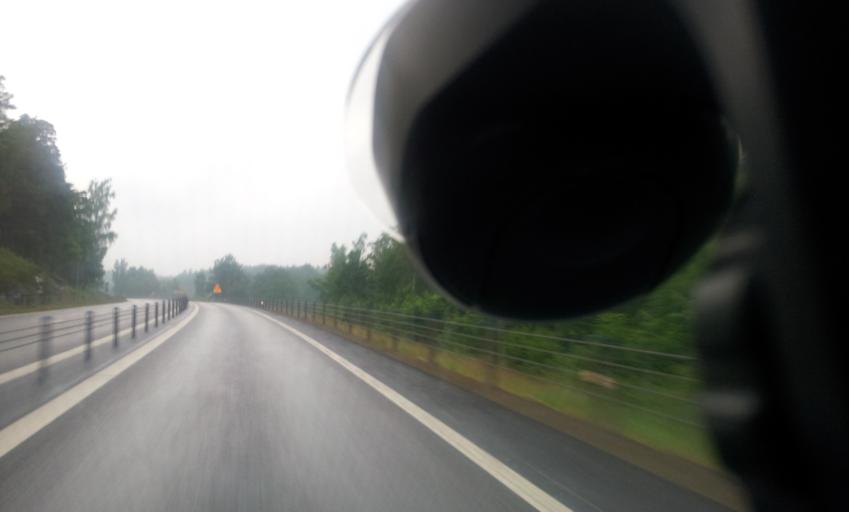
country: SE
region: Kalmar
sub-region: Vasterviks Kommun
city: Gamleby
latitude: 57.8478
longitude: 16.4356
